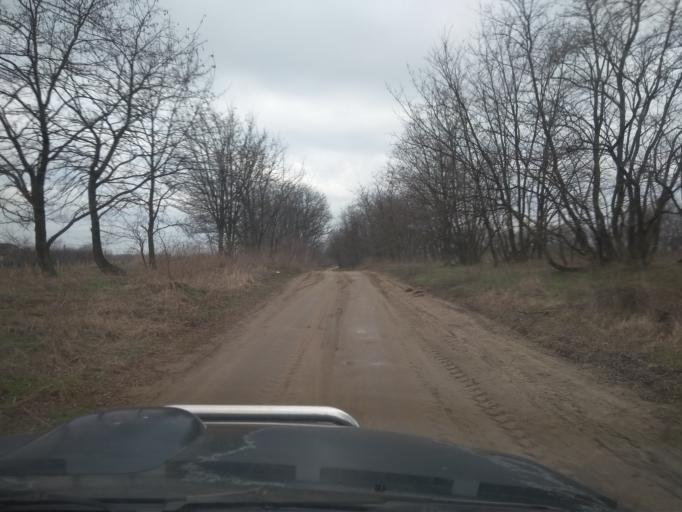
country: HU
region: Szabolcs-Szatmar-Bereg
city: Nyiregyhaza
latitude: 47.9650
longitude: 21.6716
